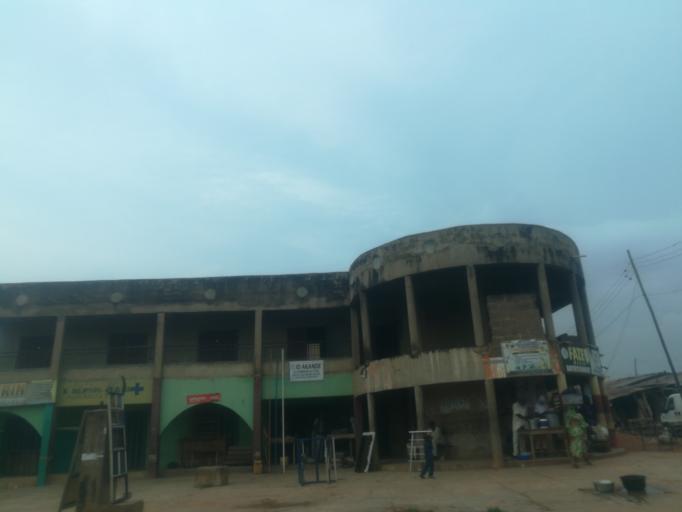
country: NG
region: Oyo
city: Ibadan
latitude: 7.4358
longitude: 3.9192
